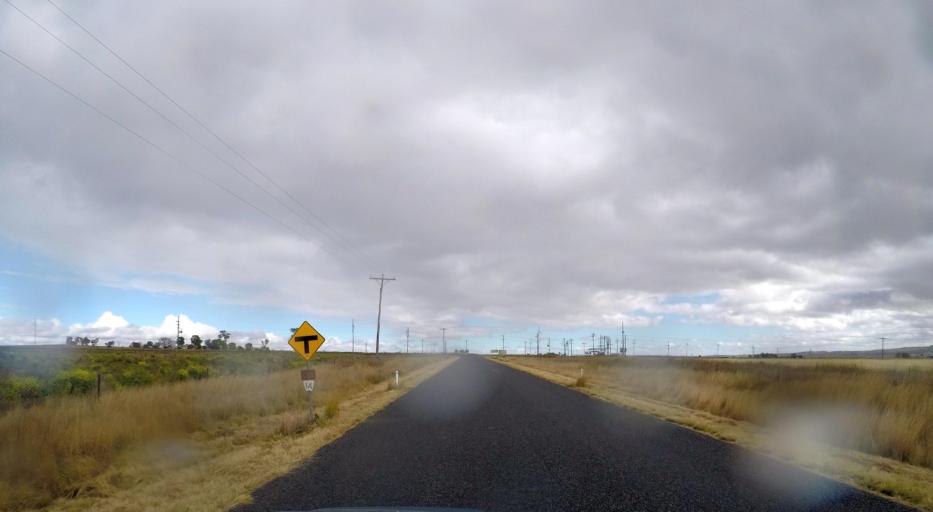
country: AU
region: Queensland
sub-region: Southern Downs
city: Warwick
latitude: -28.0577
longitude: 152.0165
